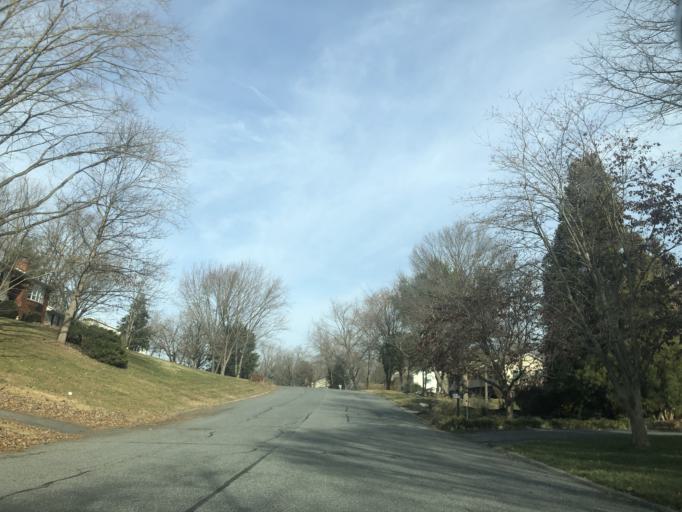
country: US
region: Maryland
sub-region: Howard County
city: Columbia
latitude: 39.2865
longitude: -76.8469
